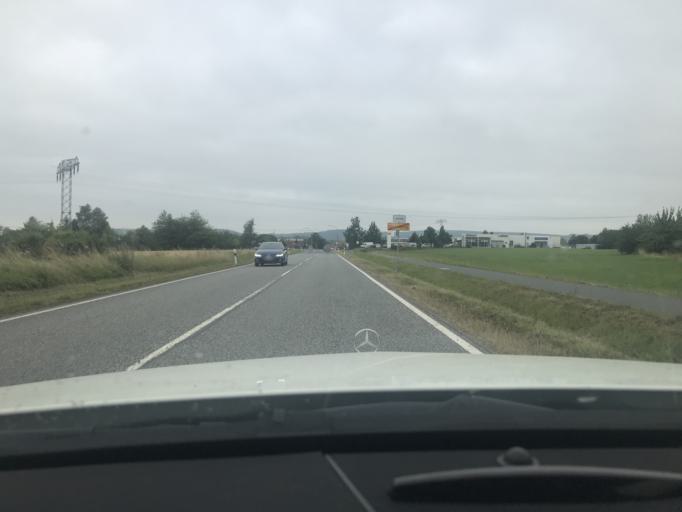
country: DE
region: Thuringia
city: Leinefelde
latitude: 51.3971
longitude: 10.3293
